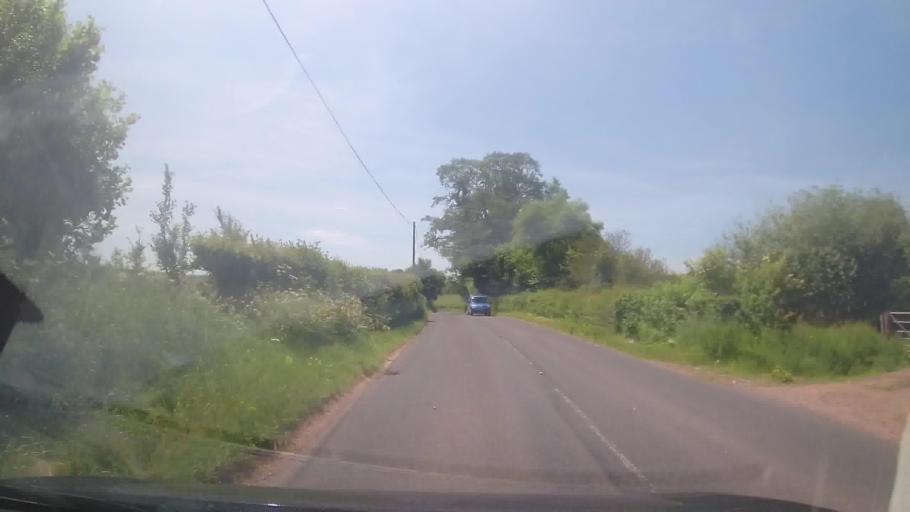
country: GB
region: England
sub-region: Herefordshire
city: Llanrothal
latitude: 51.8663
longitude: -2.7326
